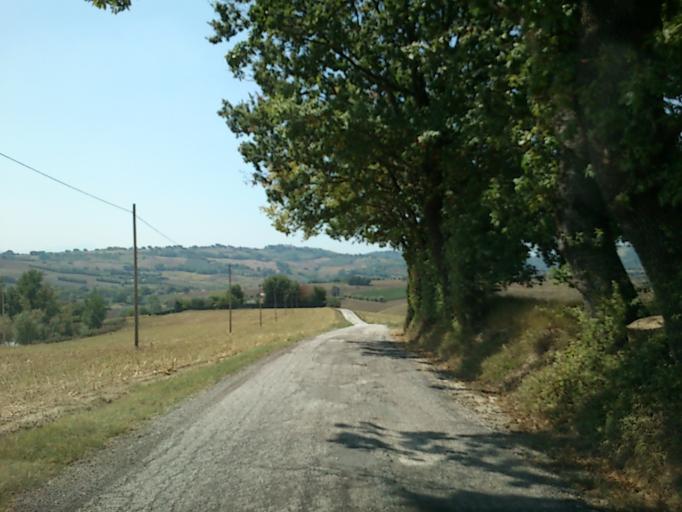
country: IT
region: The Marches
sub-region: Provincia di Pesaro e Urbino
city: Lucrezia
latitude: 43.7876
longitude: 12.9229
